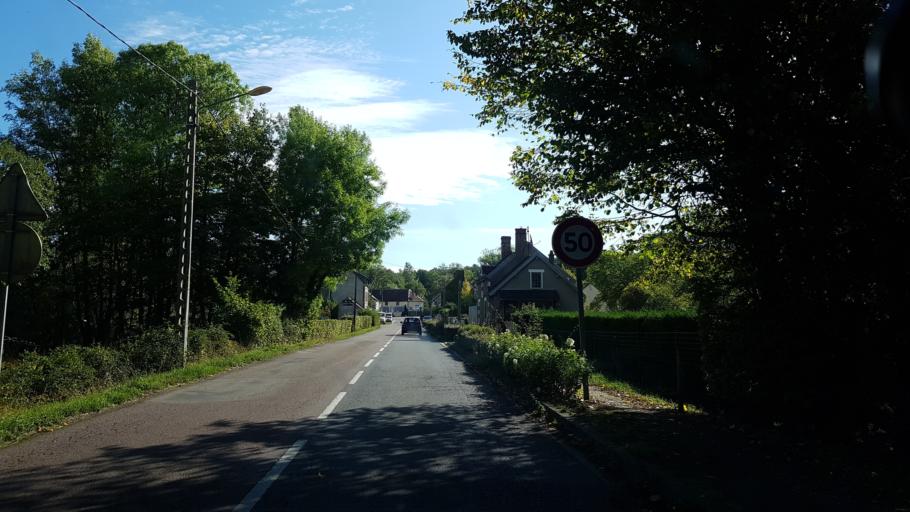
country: FR
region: Bourgogne
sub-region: Departement de la Nievre
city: Saint-Amand-en-Puisaye
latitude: 47.5326
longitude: 3.0694
